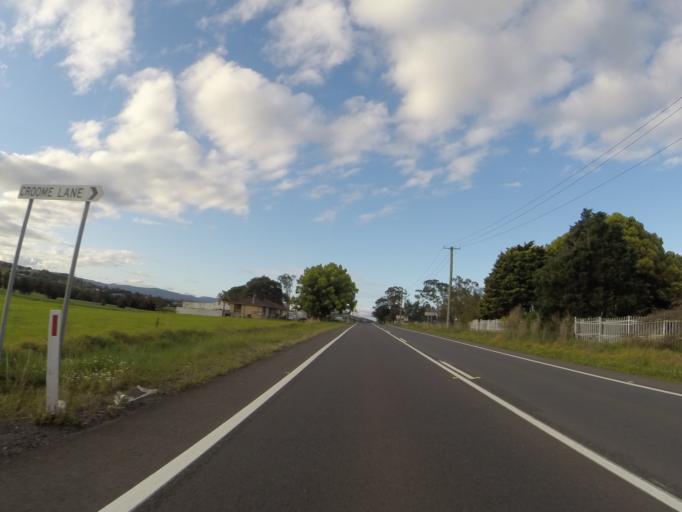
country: AU
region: New South Wales
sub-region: Shellharbour
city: Albion Park Rail
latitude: -34.5538
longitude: 150.7817
